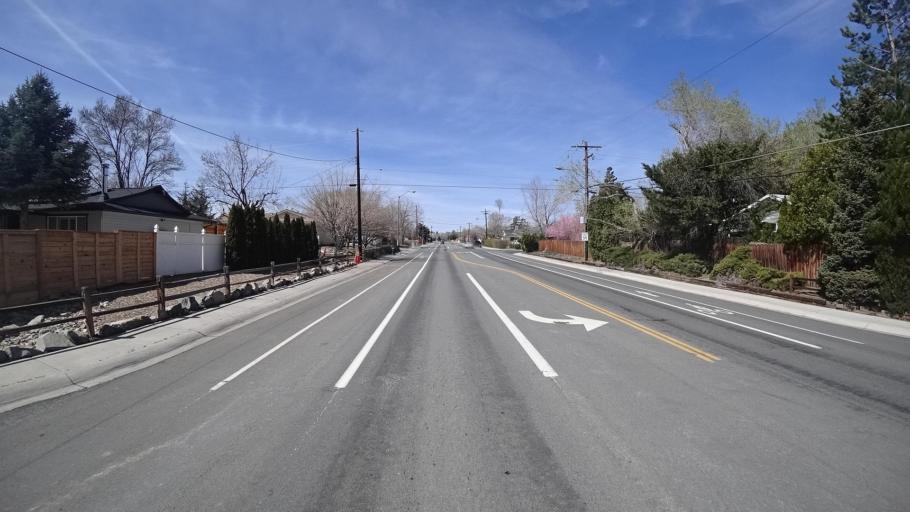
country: US
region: Nevada
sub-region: Washoe County
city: Reno
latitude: 39.5304
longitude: -119.8505
